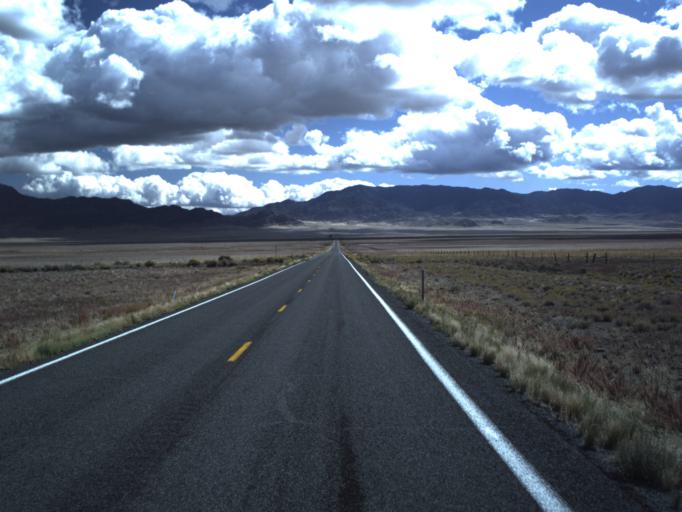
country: US
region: Utah
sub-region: Beaver County
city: Milford
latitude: 38.5551
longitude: -113.7435
